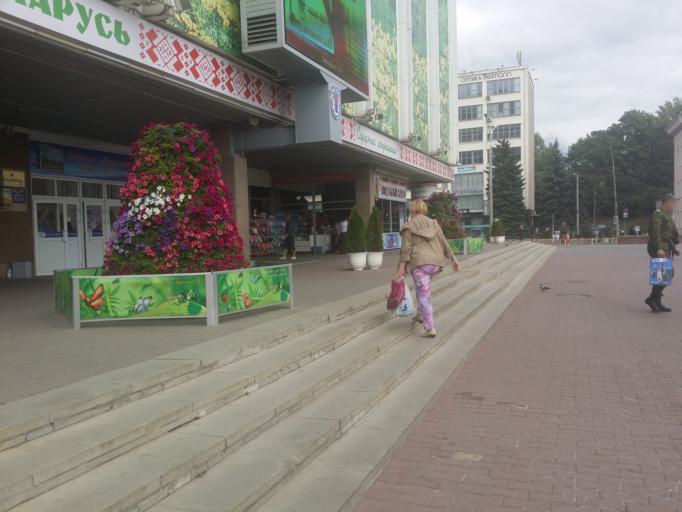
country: BY
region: Minsk
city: Minsk
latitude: 53.8760
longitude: 27.6297
